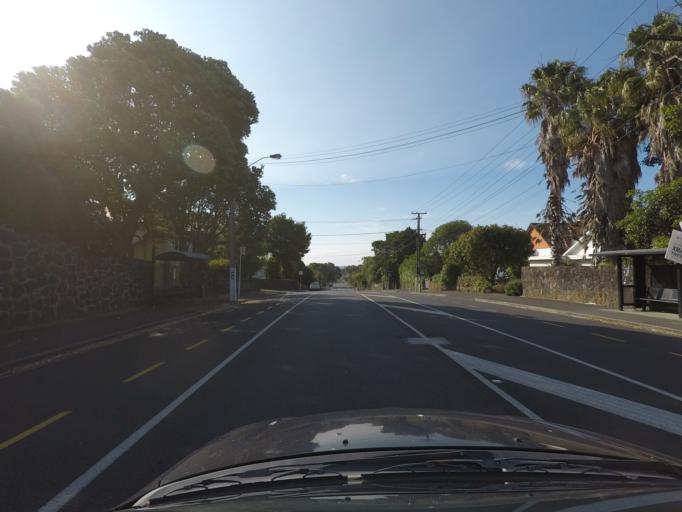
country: NZ
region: Auckland
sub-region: Auckland
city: Rosebank
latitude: -36.8866
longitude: 174.7193
